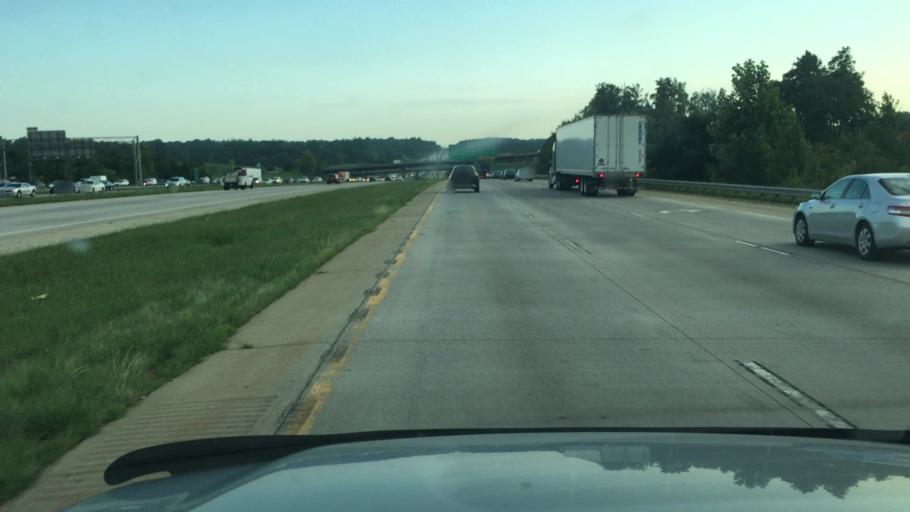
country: US
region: North Carolina
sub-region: Gaston County
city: Belmont
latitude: 35.2423
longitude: -80.9692
